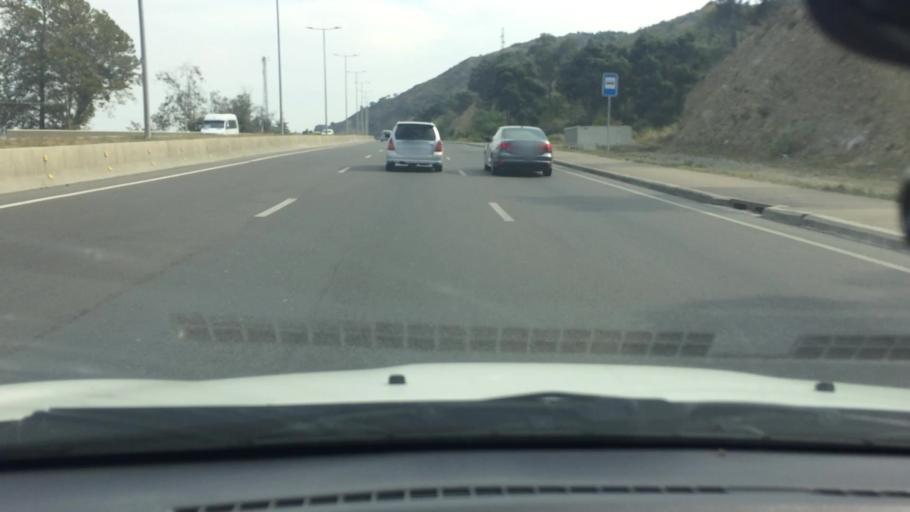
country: GE
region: T'bilisi
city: Tbilisi
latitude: 41.6655
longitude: 44.8690
